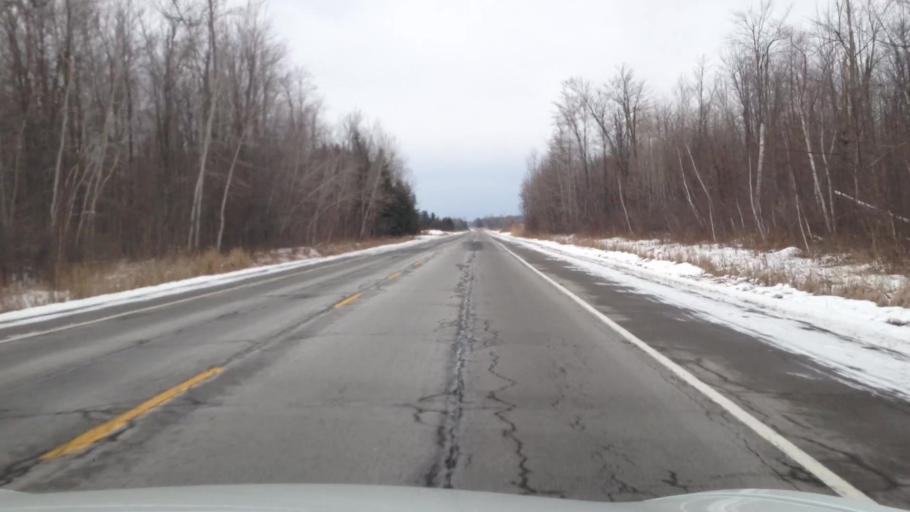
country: CA
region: Ontario
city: Clarence-Rockland
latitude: 45.3600
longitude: -75.3732
